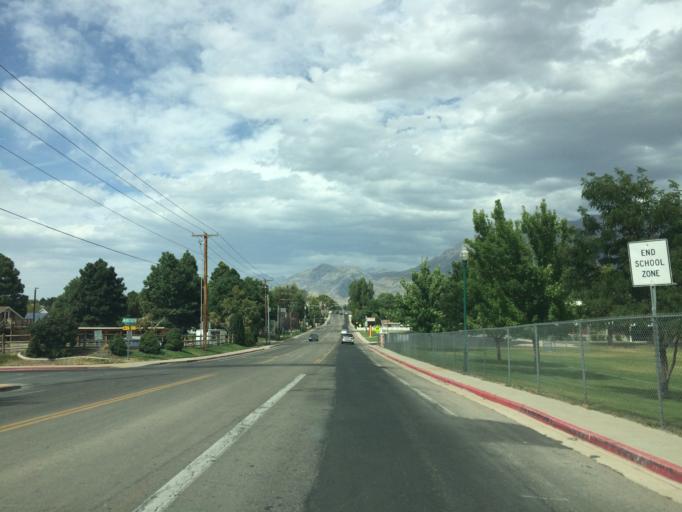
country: US
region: Utah
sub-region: Utah County
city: Orem
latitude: 40.2785
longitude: -111.7048
